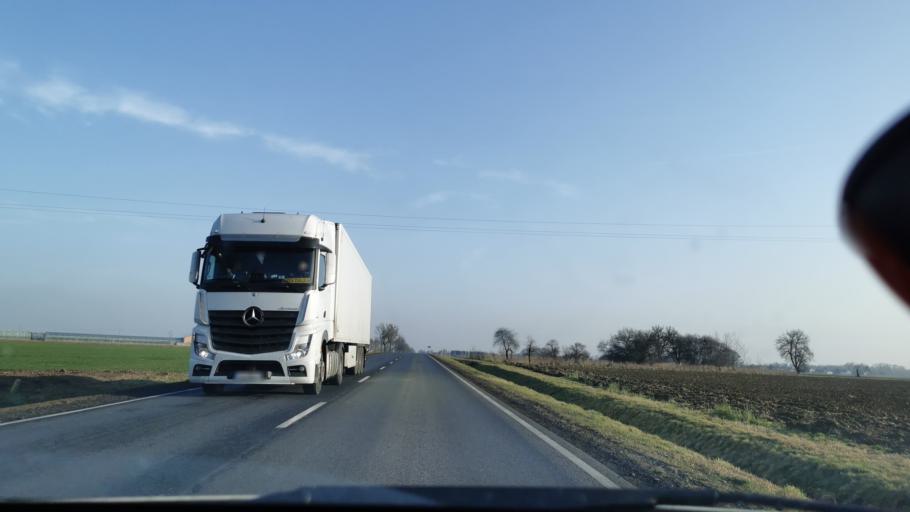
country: PL
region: Lodz Voivodeship
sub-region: Powiat sieradzki
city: Blaszki
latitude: 51.6817
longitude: 18.3397
